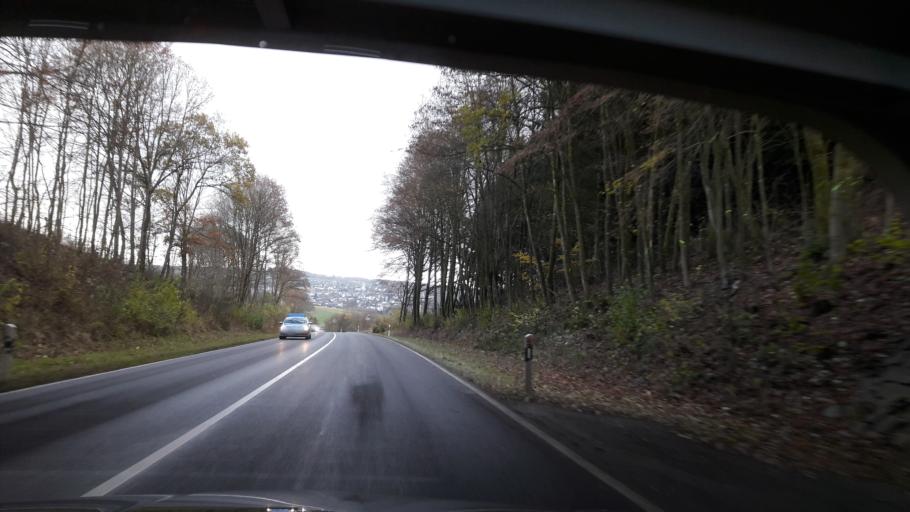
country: DE
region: Rheinland-Pfalz
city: Hermeskeil
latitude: 49.6641
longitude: 6.9170
